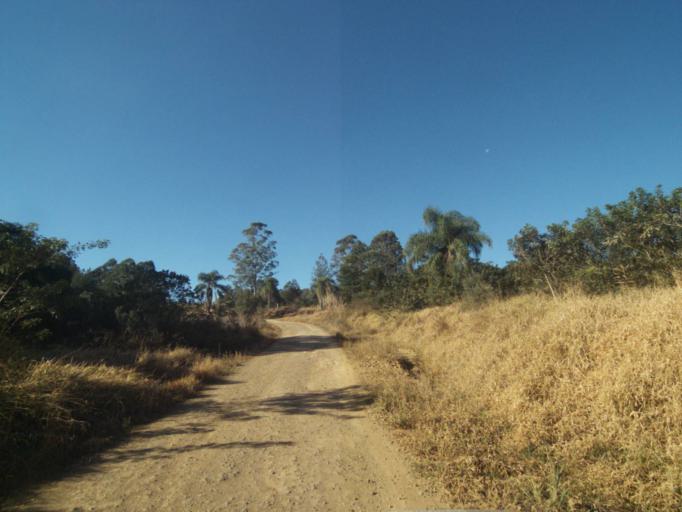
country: BR
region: Parana
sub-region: Tibagi
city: Tibagi
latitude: -24.5464
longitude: -50.5112
